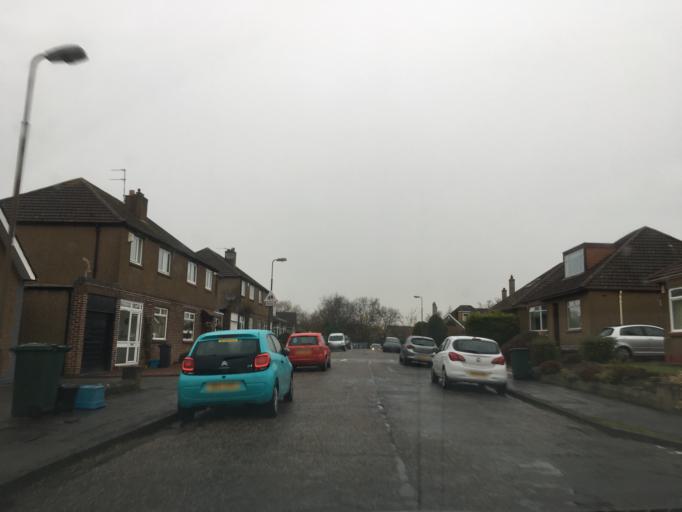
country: GB
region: Scotland
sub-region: Edinburgh
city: Currie
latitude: 55.9500
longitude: -3.3008
